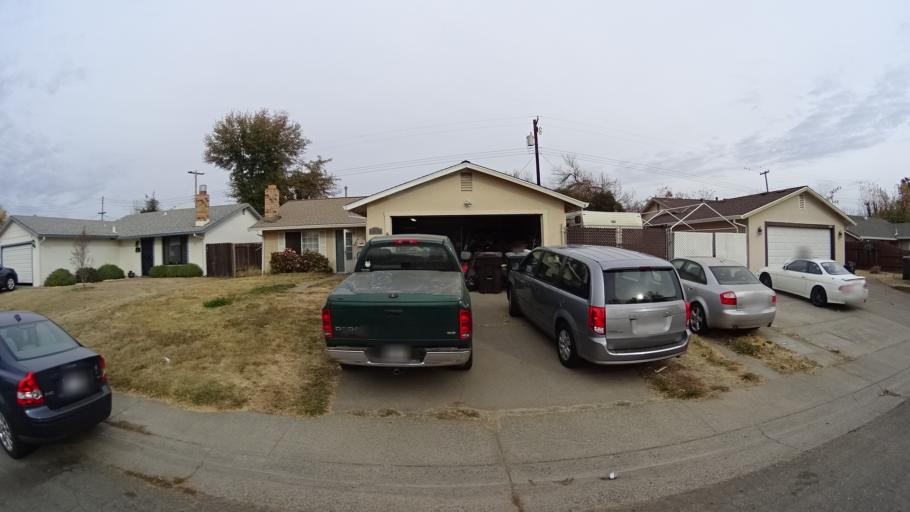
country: US
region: California
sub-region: Sacramento County
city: Citrus Heights
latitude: 38.7150
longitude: -121.2985
